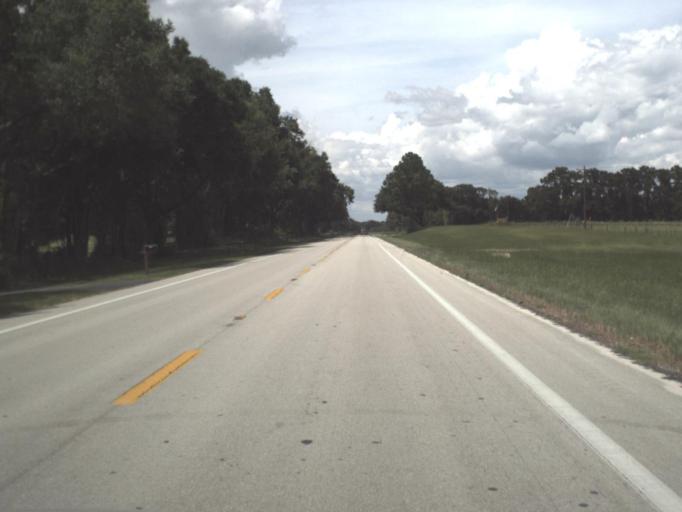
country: US
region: Florida
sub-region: Alachua County
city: High Springs
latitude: 29.7885
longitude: -82.6081
